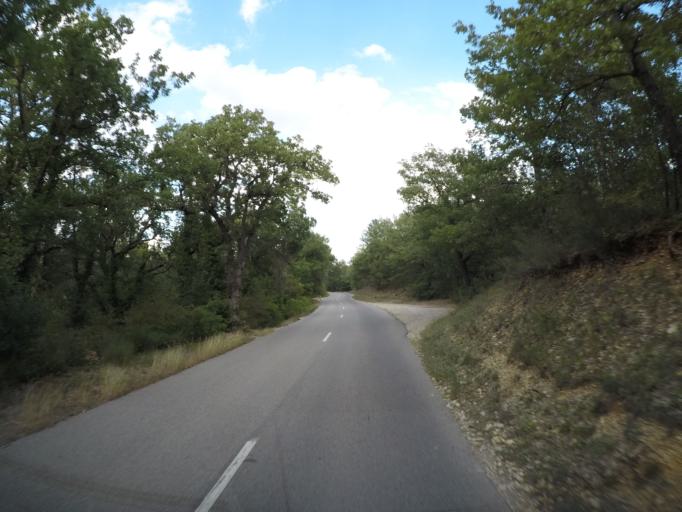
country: FR
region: Provence-Alpes-Cote d'Azur
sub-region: Departement des Alpes-de-Haute-Provence
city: Valensole
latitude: 43.8329
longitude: 6.0034
